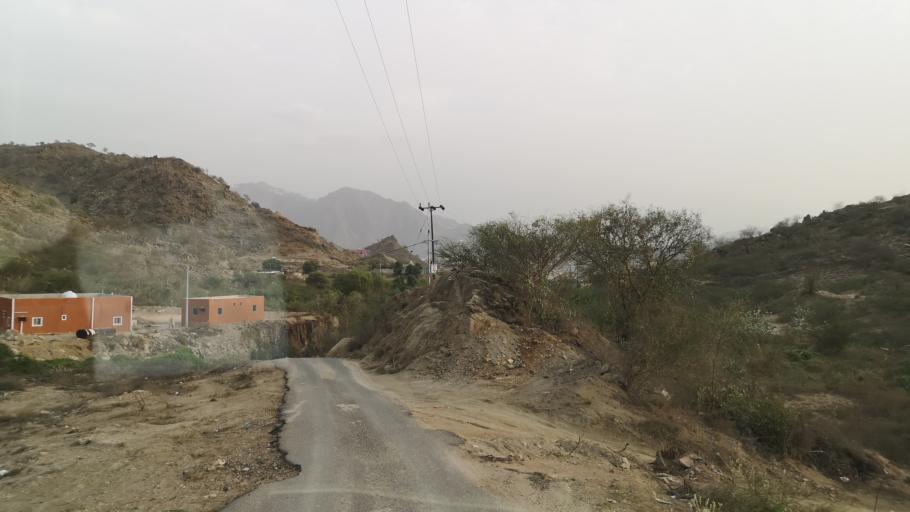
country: YE
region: Sa'dah
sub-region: Monabbih
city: Suq al Khamis
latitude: 17.3716
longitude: 43.1270
